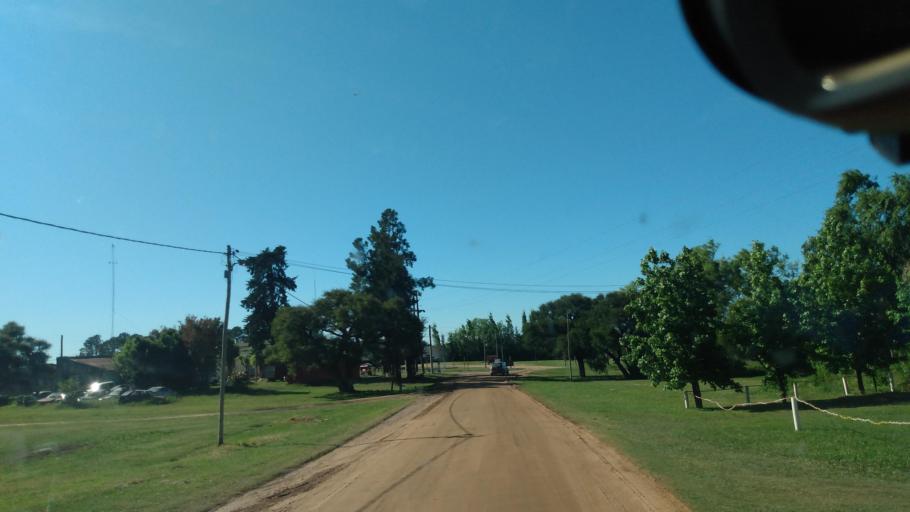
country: AR
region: Entre Rios
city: Colon
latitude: -32.1541
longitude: -58.1959
